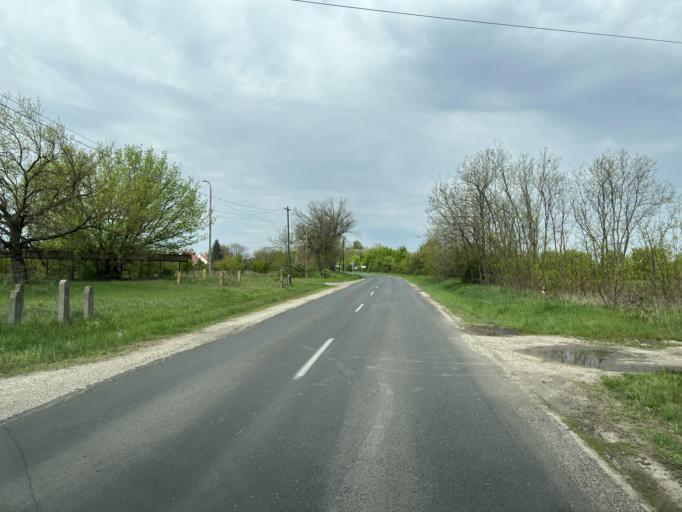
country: HU
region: Pest
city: Cegled
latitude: 47.1647
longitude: 19.8374
